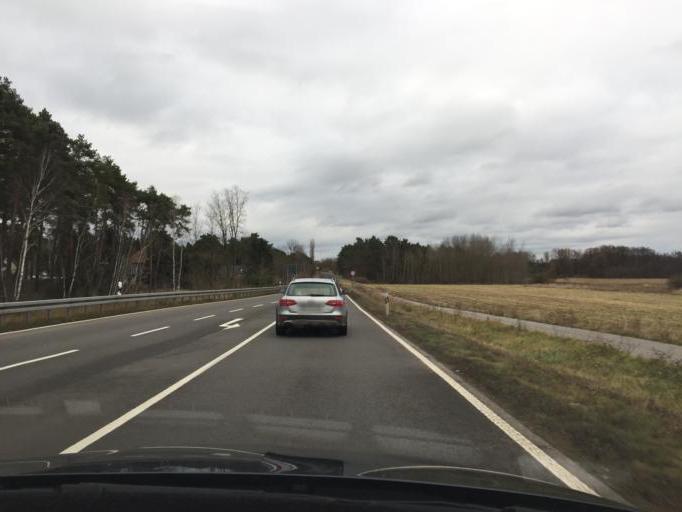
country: DE
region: Brandenburg
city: Ziltendorf
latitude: 52.1954
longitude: 14.6033
